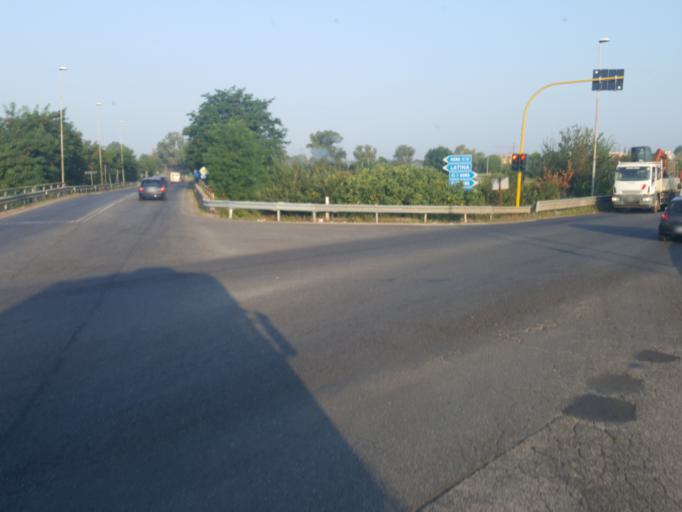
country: IT
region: Latium
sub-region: Provincia di Latina
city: Borgo San Michele
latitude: 41.4633
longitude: 13.0027
